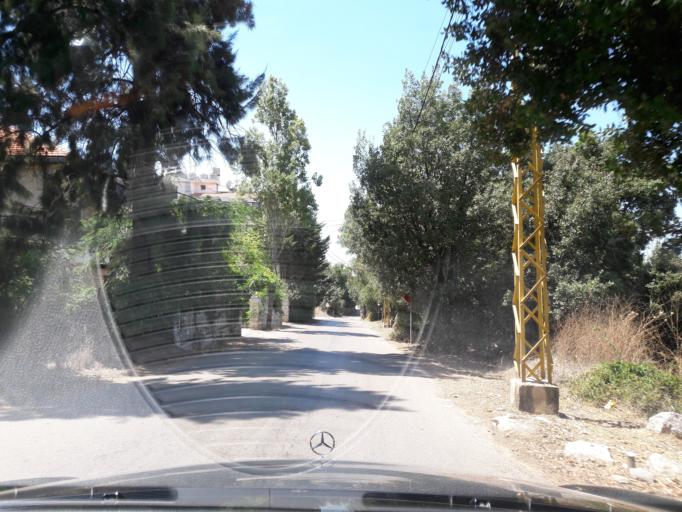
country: LB
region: Mont-Liban
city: Djounie
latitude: 33.9252
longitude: 35.6483
